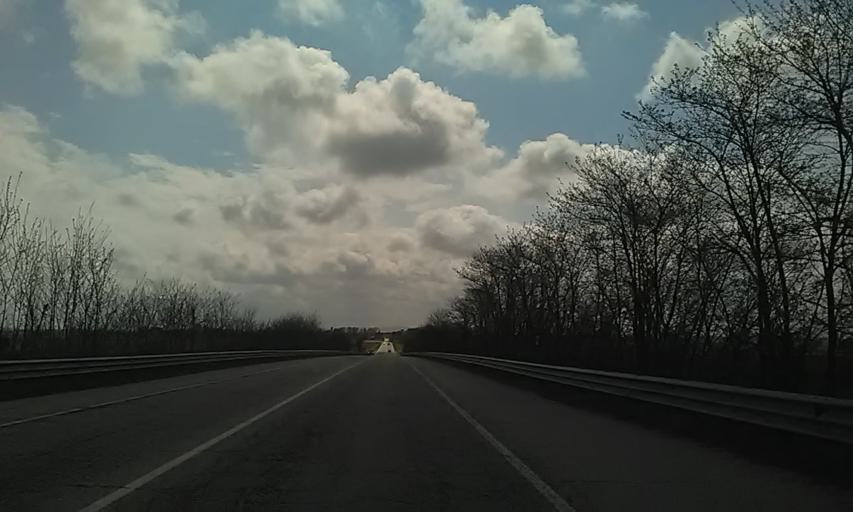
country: IT
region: Piedmont
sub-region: Provincia di Vercelli
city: Stroppiana
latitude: 45.2466
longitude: 8.4592
